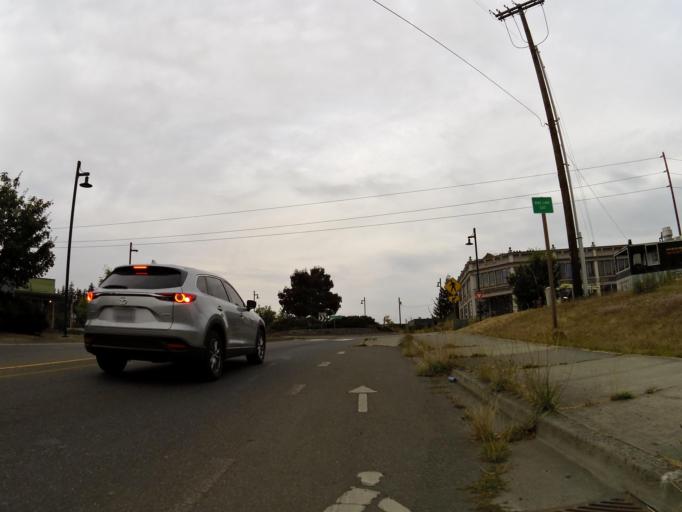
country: US
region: Washington
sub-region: Jefferson County
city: Port Townsend
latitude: 48.1035
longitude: -122.7981
